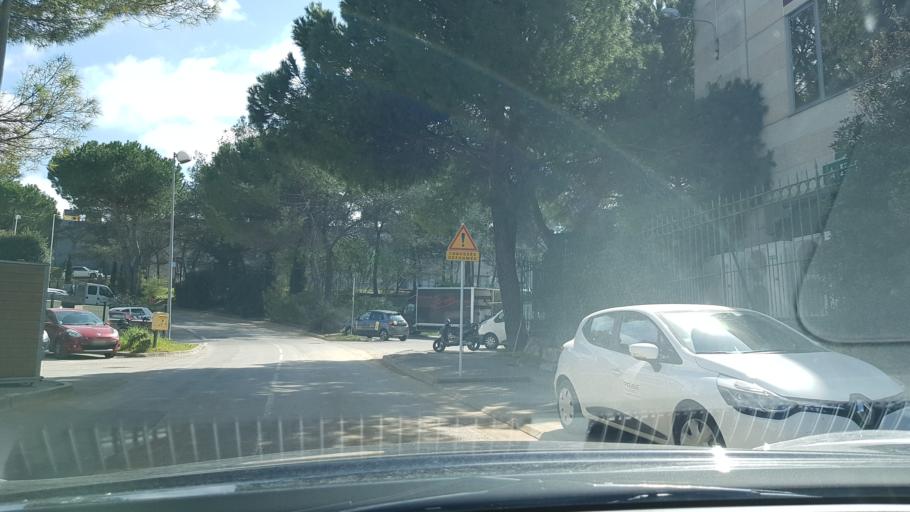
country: FR
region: Provence-Alpes-Cote d'Azur
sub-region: Departement des Alpes-Maritimes
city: Biot
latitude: 43.6093
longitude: 7.0736
